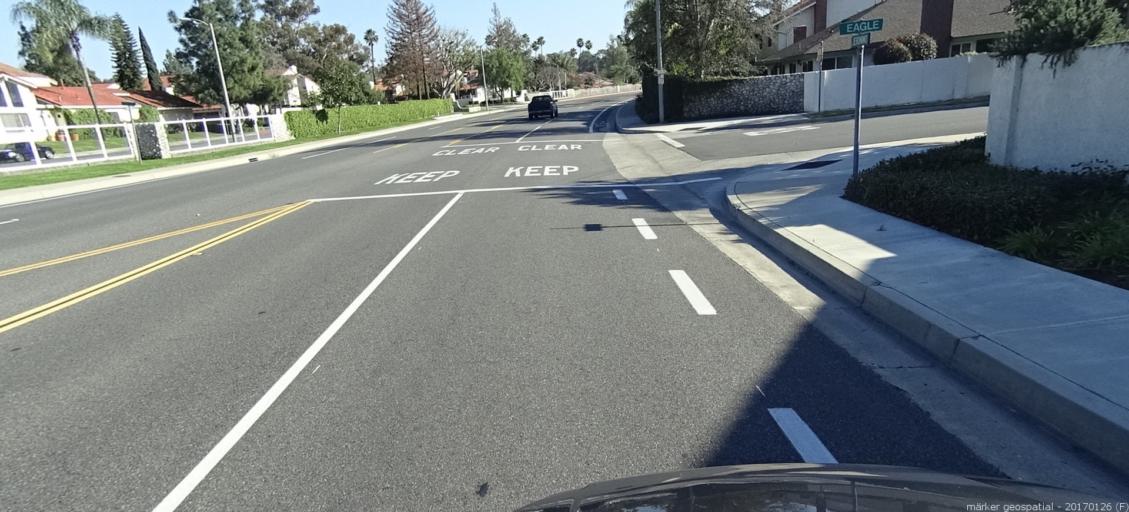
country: US
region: California
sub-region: Orange County
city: Lake Forest
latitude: 33.6434
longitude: -117.7057
